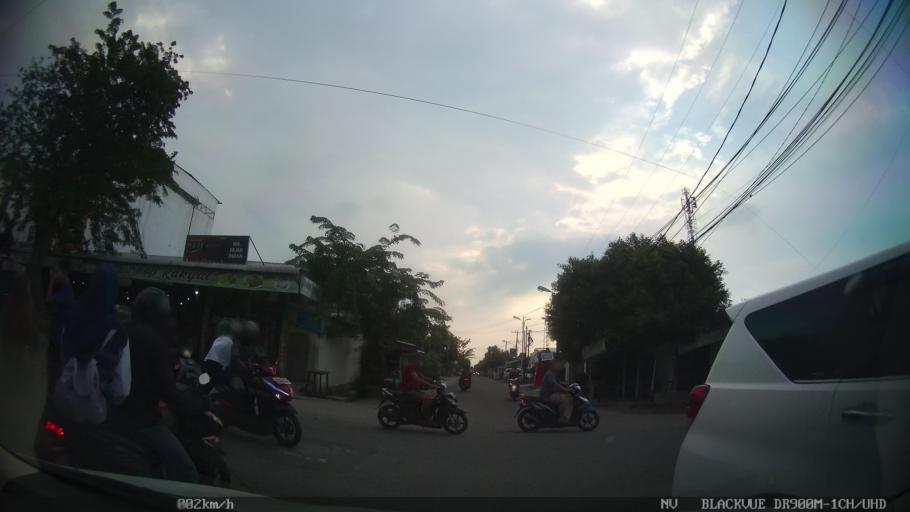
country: ID
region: North Sumatra
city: Medan
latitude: 3.6097
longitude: 98.6915
